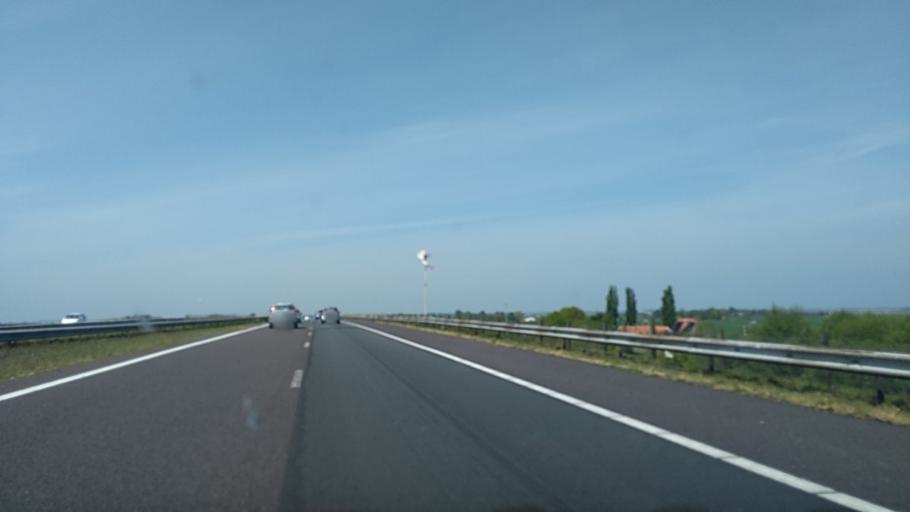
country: NL
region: Friesland
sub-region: Gemeente Skarsterlan
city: Joure
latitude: 52.9731
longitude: 5.7573
